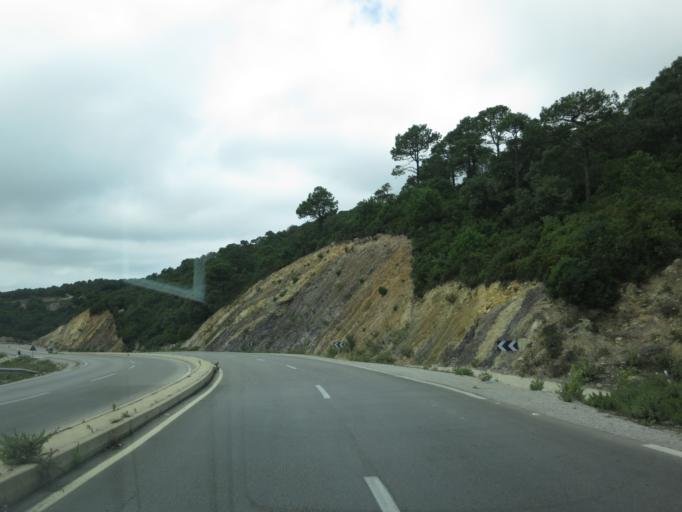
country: ES
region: Ceuta
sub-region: Ceuta
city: Ceuta
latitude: 35.8765
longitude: -5.4003
